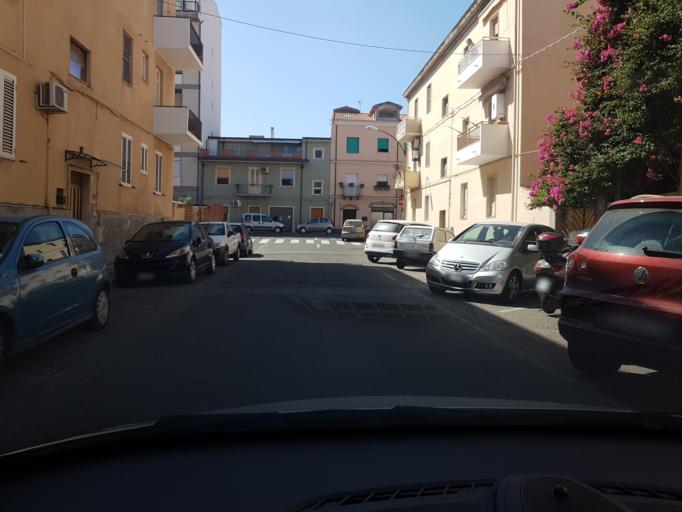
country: IT
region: Sardinia
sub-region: Provincia di Oristano
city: Oristano
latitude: 39.9090
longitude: 8.5923
